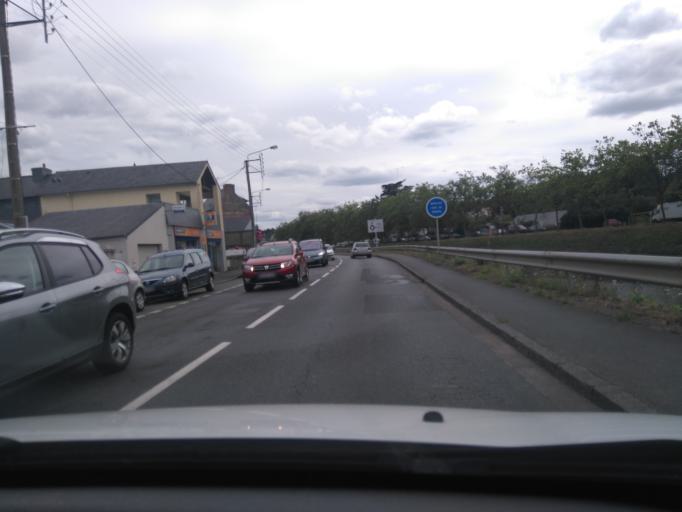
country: FR
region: Brittany
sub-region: Departement des Cotes-d'Armor
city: Lannion
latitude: 48.7333
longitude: -3.4674
